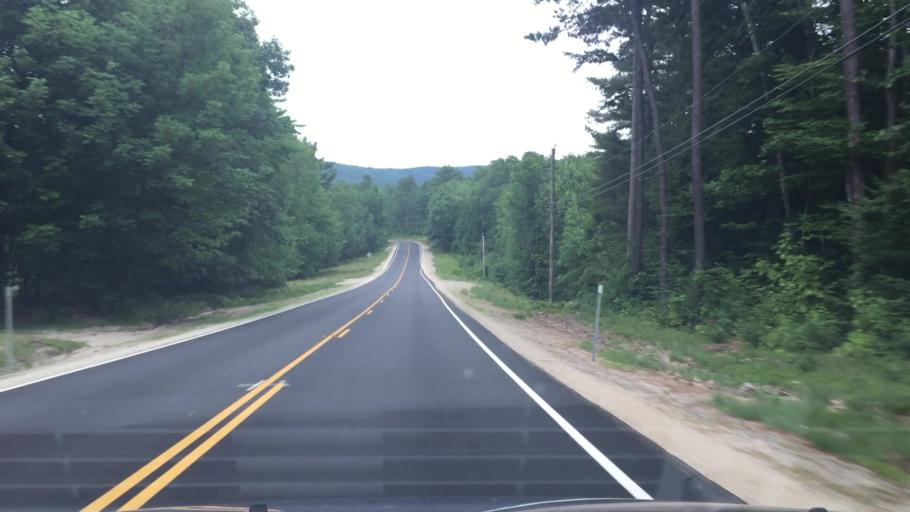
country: US
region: New Hampshire
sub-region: Carroll County
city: Freedom
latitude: 43.8123
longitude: -71.0664
